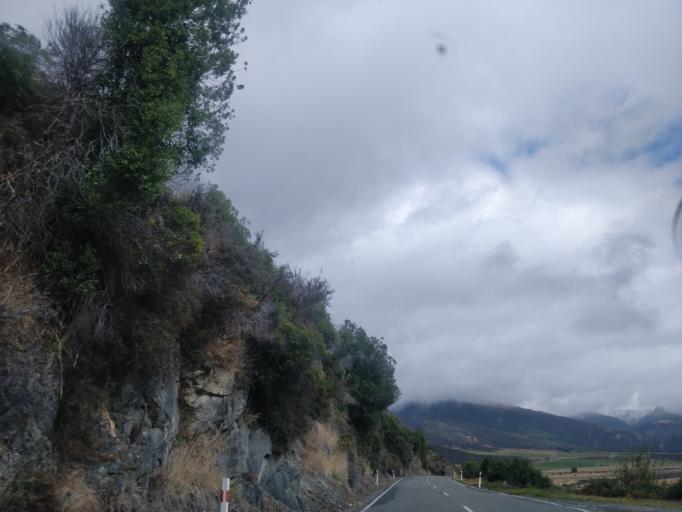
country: NZ
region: Canterbury
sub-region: Waimakariri District
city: Oxford
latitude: -43.0255
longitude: 171.6950
